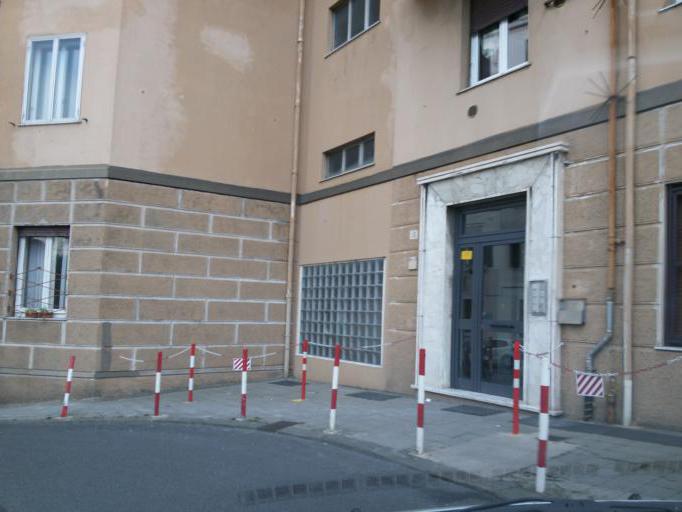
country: IT
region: Liguria
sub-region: Provincia di Genova
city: Genoa
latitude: 44.4098
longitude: 8.9479
